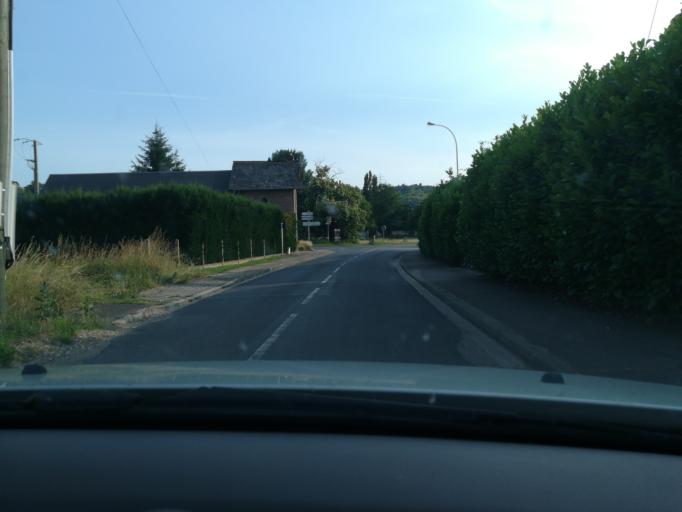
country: FR
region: Haute-Normandie
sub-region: Departement de la Seine-Maritime
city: Sahurs
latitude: 49.3588
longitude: 0.9459
